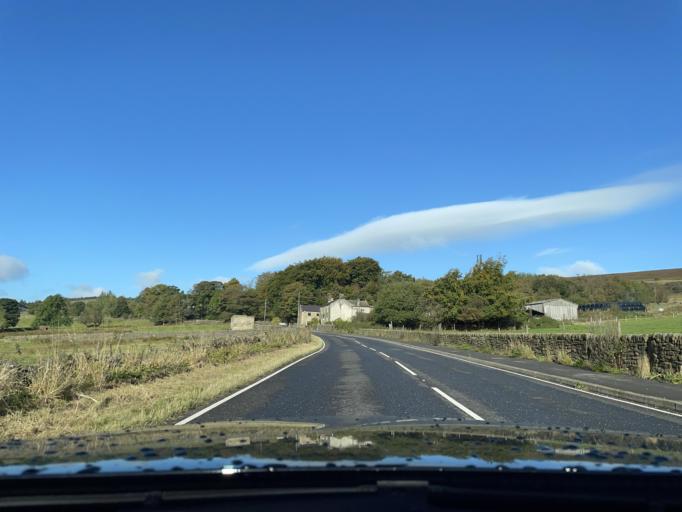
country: GB
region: England
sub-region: Sheffield
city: Bradfield
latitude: 53.3853
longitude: -1.6112
